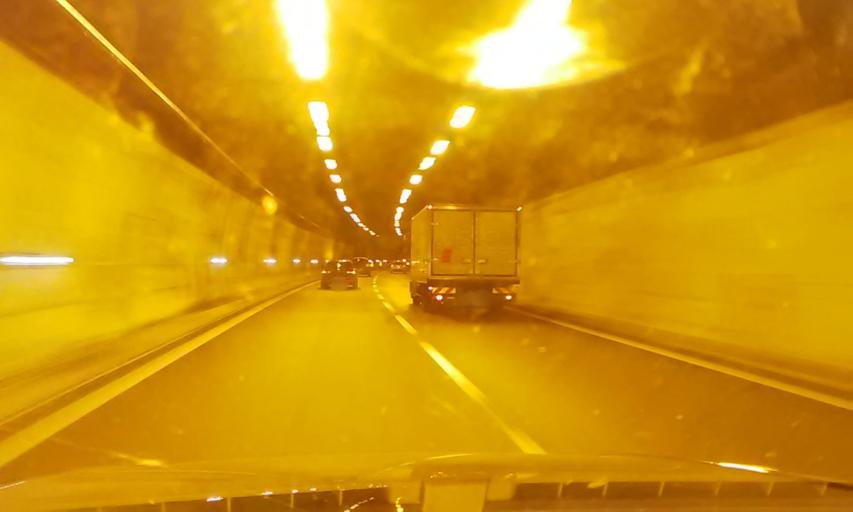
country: IT
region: Liguria
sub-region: Provincia di Savona
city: Tovo San Giacomo
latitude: 44.1681
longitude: 8.2788
